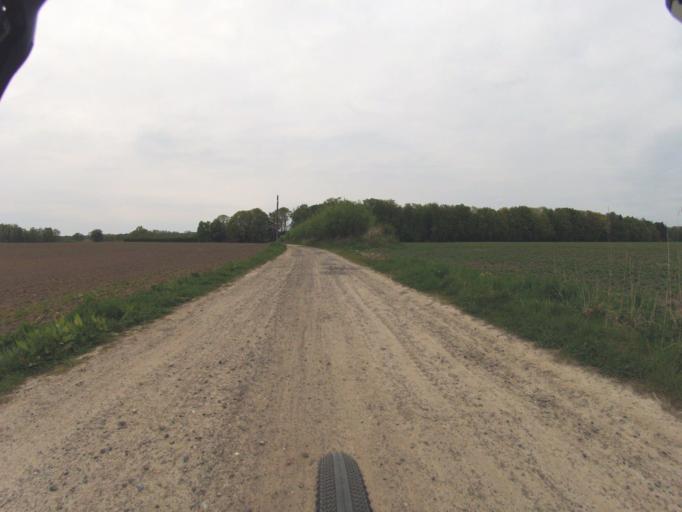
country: DE
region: North Rhine-Westphalia
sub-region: Regierungsbezirk Munster
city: Westerkappeln
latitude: 52.3132
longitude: 7.8366
